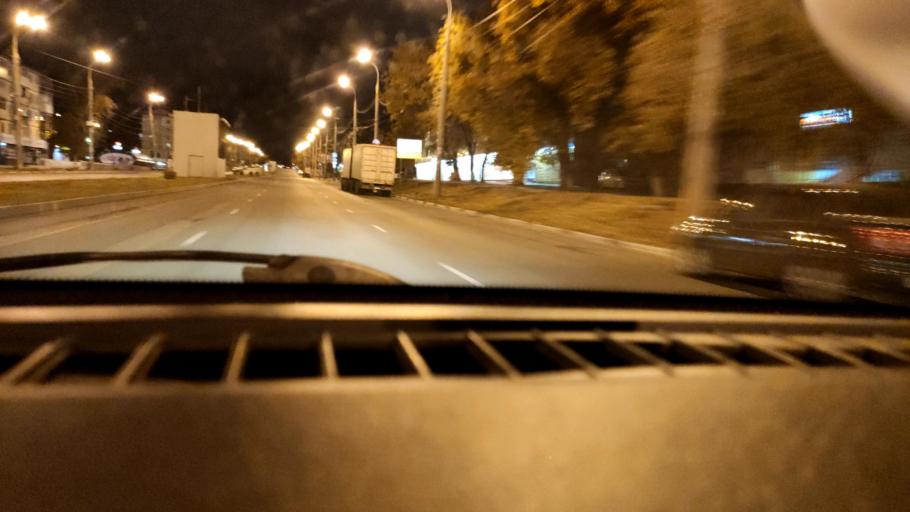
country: RU
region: Samara
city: Samara
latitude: 53.2011
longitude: 50.2020
